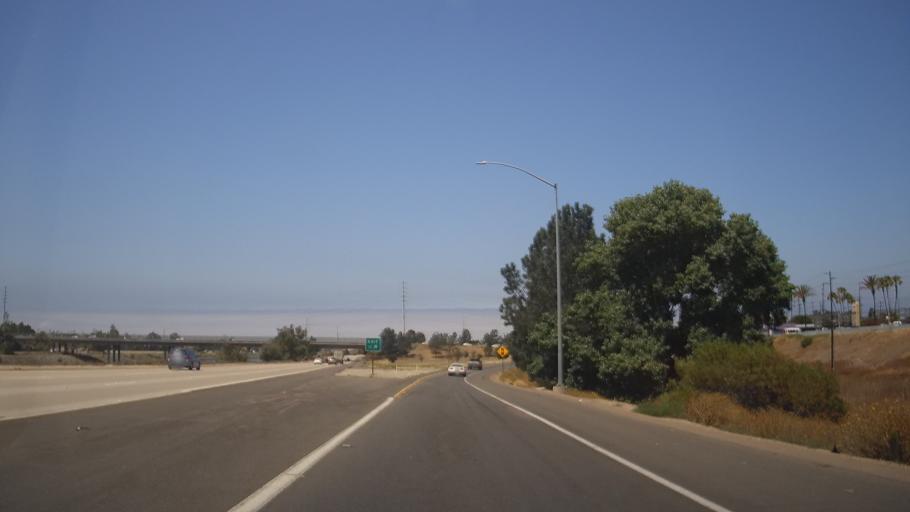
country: US
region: California
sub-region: San Diego County
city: Chula Vista
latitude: 32.6580
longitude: -117.0869
